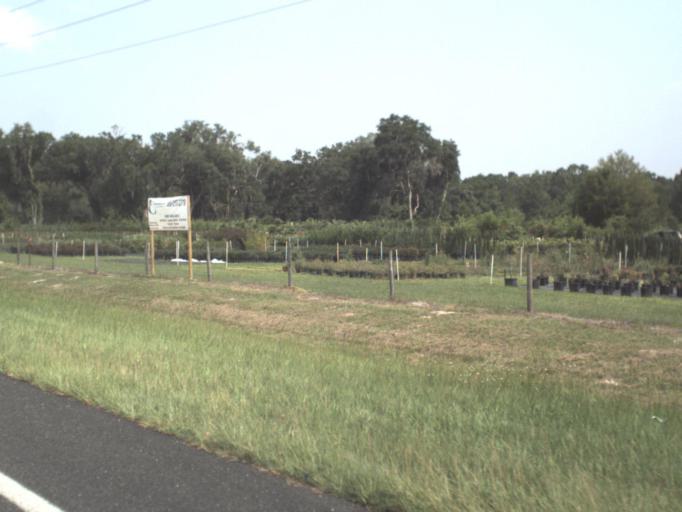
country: US
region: Florida
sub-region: Levy County
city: Williston
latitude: 29.4000
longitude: -82.5030
